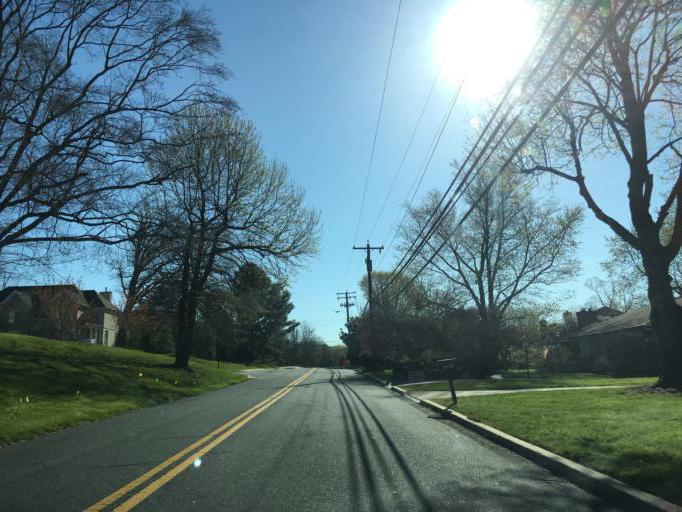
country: US
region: Maryland
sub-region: Baltimore County
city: Lutherville
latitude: 39.4113
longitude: -76.6331
